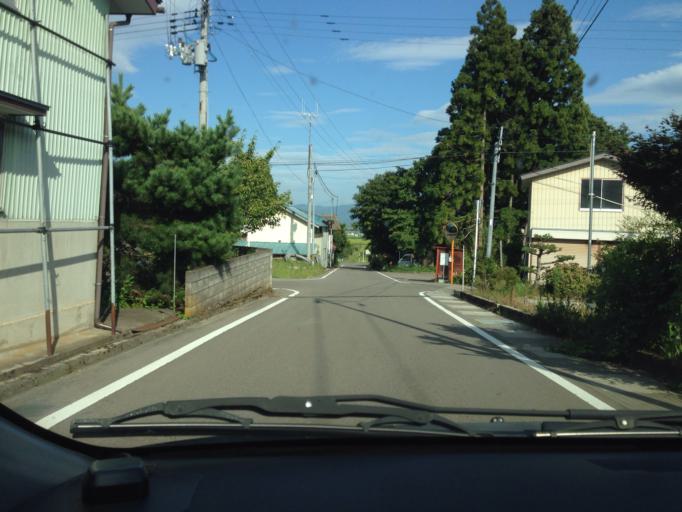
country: JP
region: Fukushima
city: Kitakata
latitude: 37.4882
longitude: 139.8175
